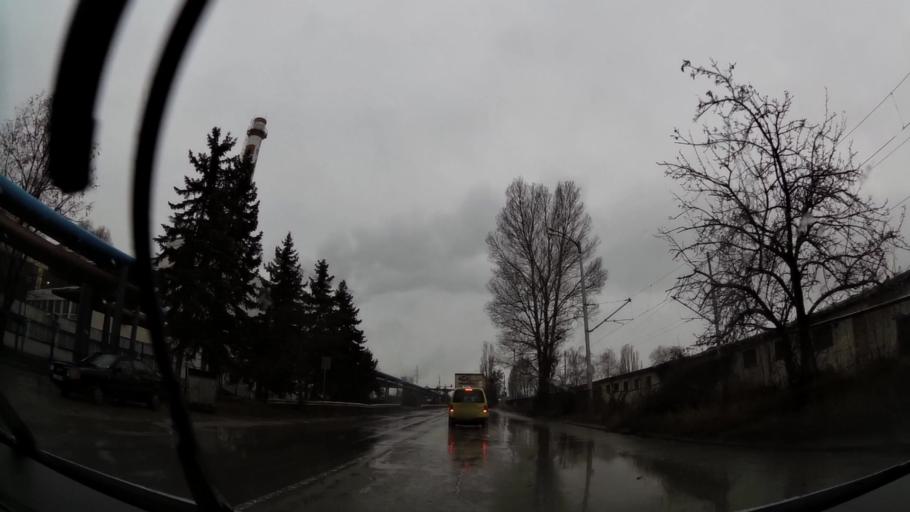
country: BG
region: Sofia-Capital
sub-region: Stolichna Obshtina
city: Sofia
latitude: 42.6581
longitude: 23.4149
